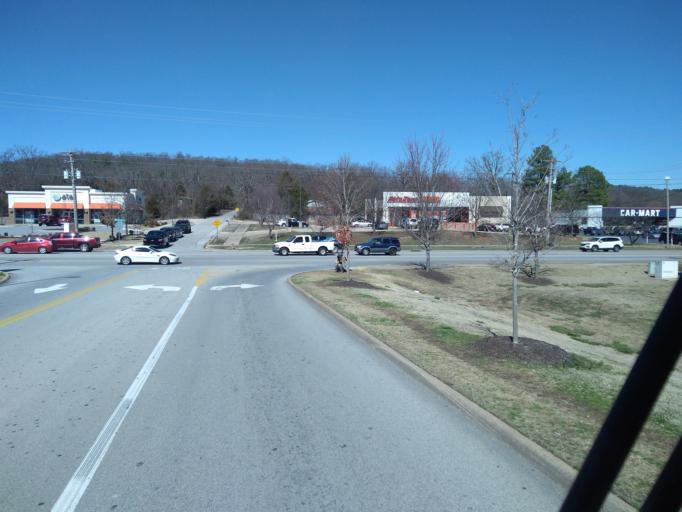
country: US
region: Arkansas
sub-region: Washington County
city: Fayetteville
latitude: 36.0521
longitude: -94.1999
